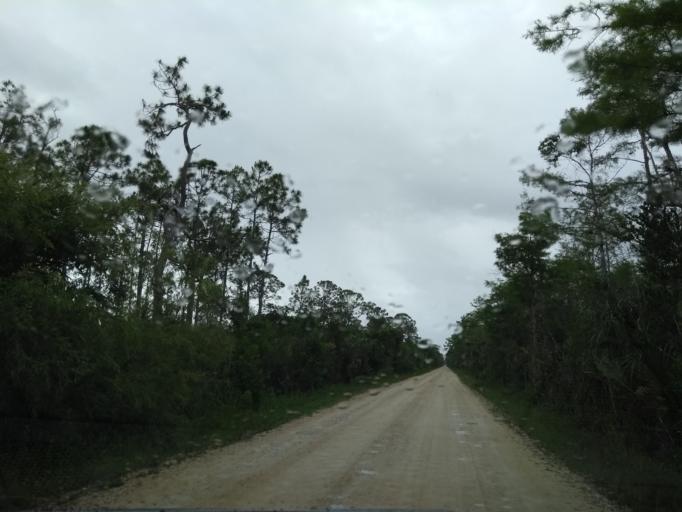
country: US
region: Florida
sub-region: Miami-Dade County
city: The Hammocks
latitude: 25.7605
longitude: -81.0020
